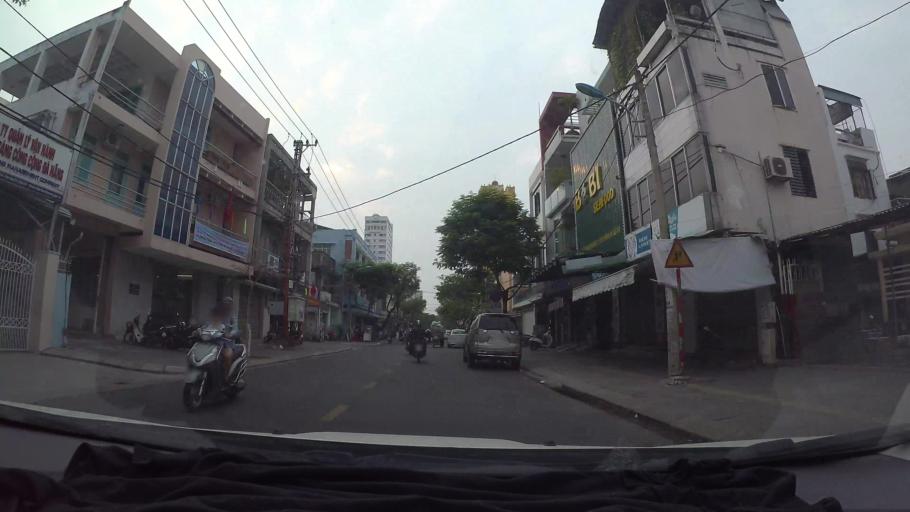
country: VN
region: Da Nang
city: Da Nang
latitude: 16.0639
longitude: 108.2221
